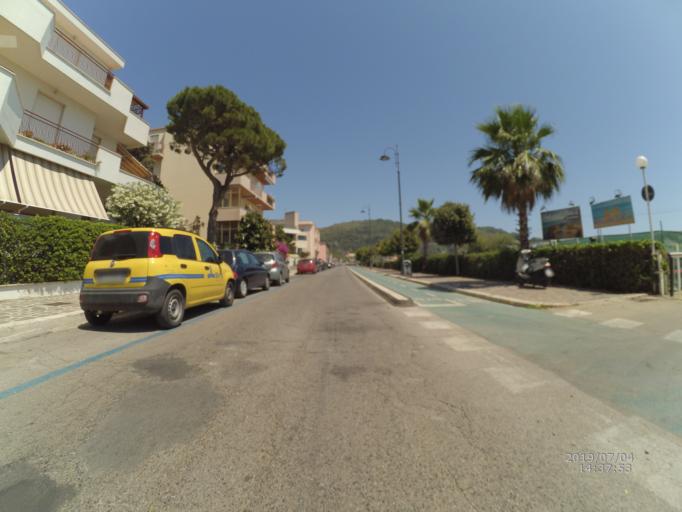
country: IT
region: Latium
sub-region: Provincia di Latina
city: Gaeta
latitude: 41.2113
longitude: 13.5643
